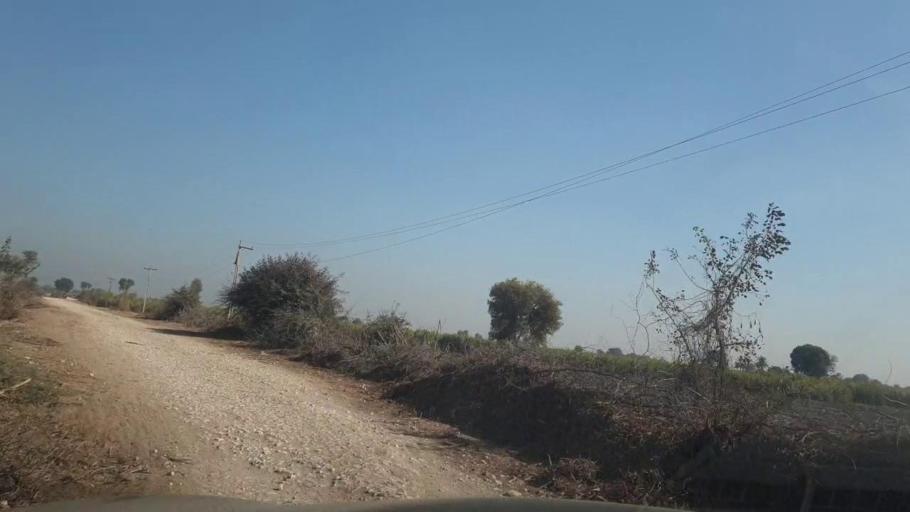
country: PK
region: Sindh
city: Mirpur Mathelo
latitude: 28.1217
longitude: 69.4921
